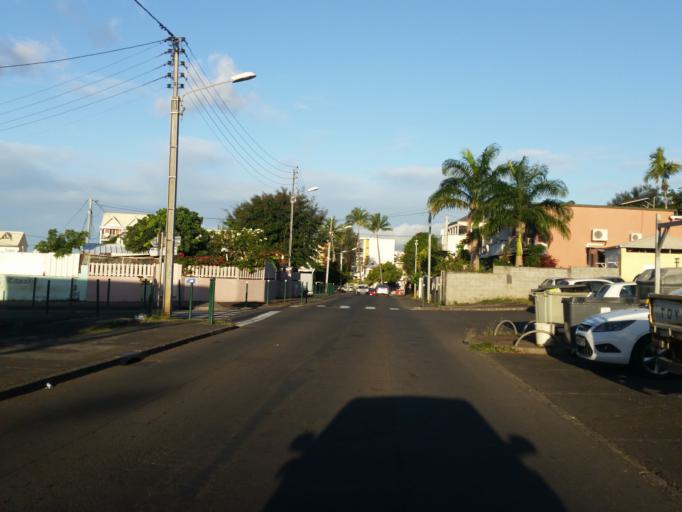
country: RE
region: Reunion
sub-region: Reunion
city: Saint-Denis
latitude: -20.8909
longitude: 55.4488
